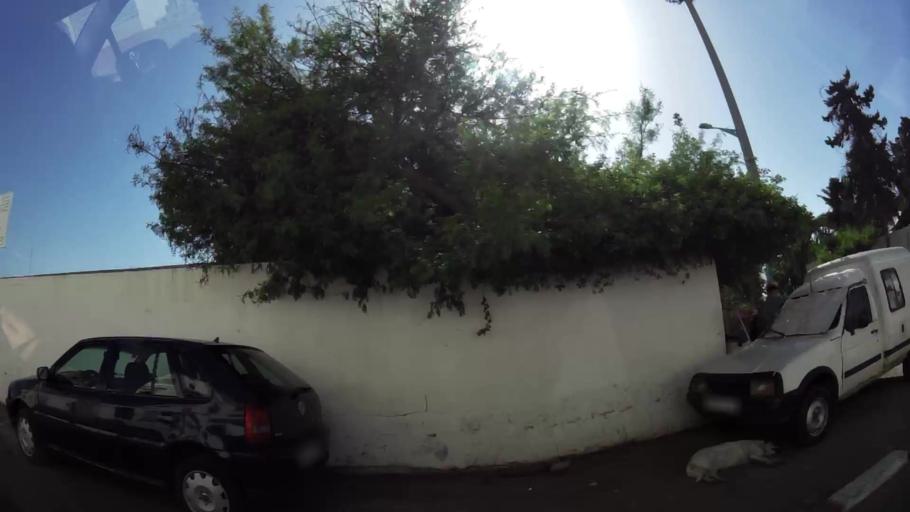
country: MA
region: Souss-Massa-Draa
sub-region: Agadir-Ida-ou-Tnan
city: Agadir
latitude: 30.4126
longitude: -9.5857
